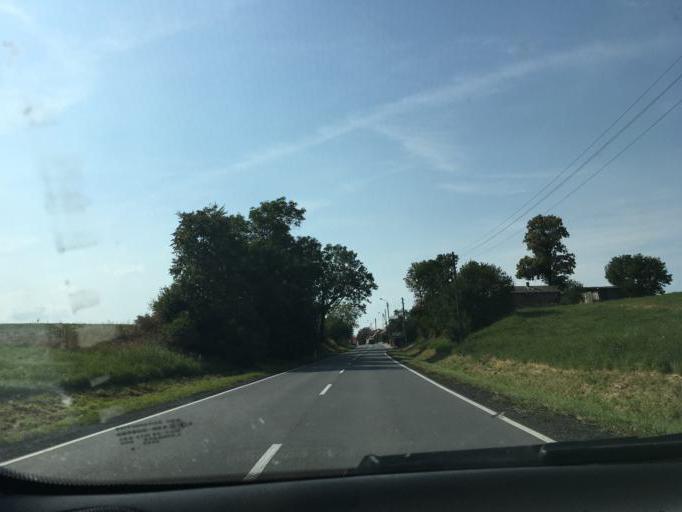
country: PL
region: Opole Voivodeship
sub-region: Powiat nyski
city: Nysa
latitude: 50.4236
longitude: 17.4385
